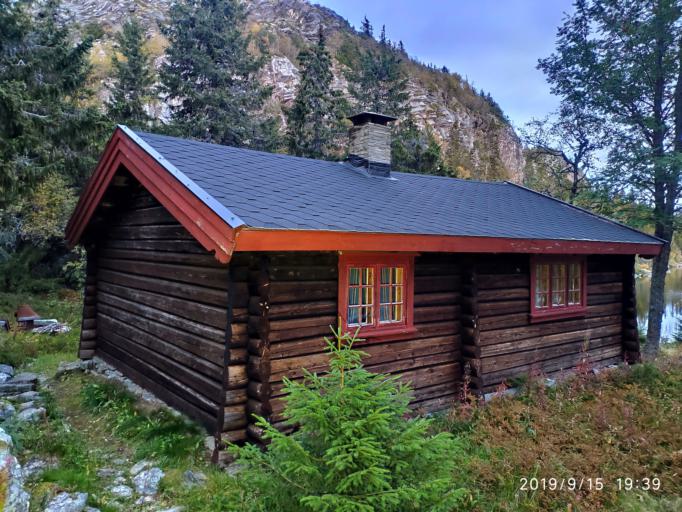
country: NO
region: Oppland
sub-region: Oyer
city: Tretten
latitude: 61.4238
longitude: 10.2635
